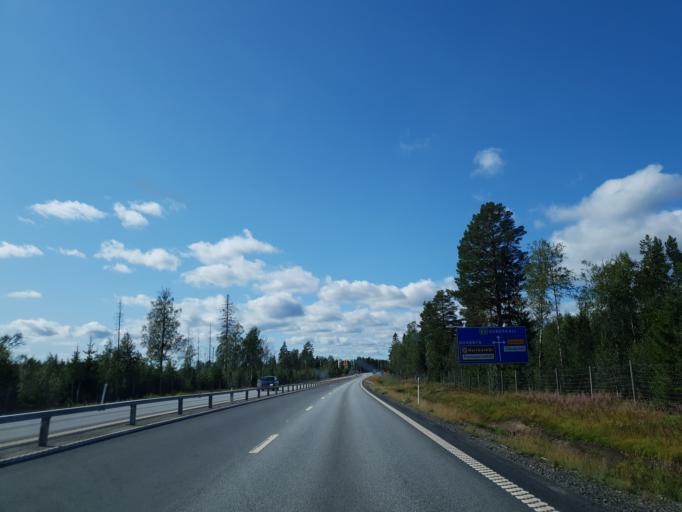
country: SE
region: Vaesterbotten
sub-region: Umea Kommun
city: Hoernefors
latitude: 63.6318
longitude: 19.8847
